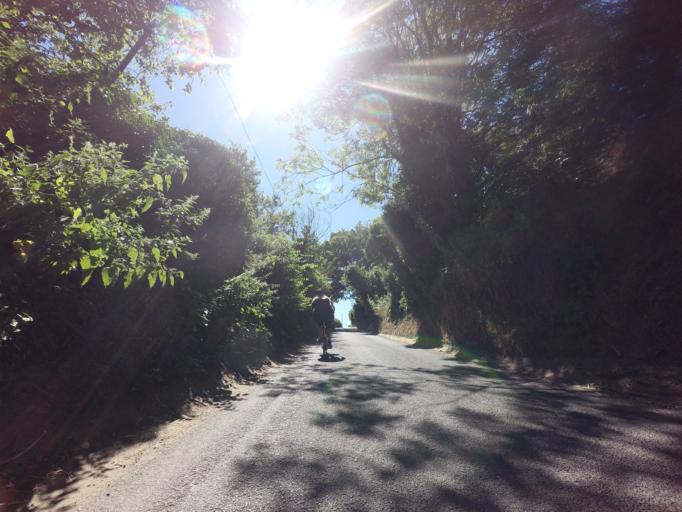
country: GB
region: England
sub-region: Kent
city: Eastry
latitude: 51.2668
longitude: 1.3035
